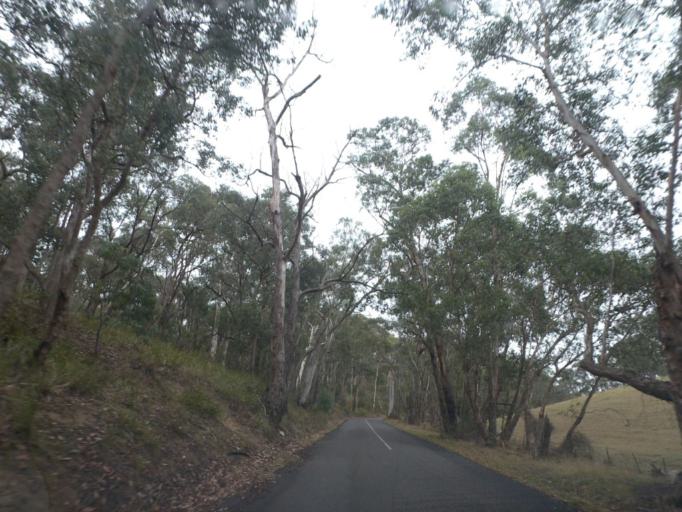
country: AU
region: Victoria
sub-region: Nillumbik
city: Saint Andrews
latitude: -37.6212
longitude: 145.2695
